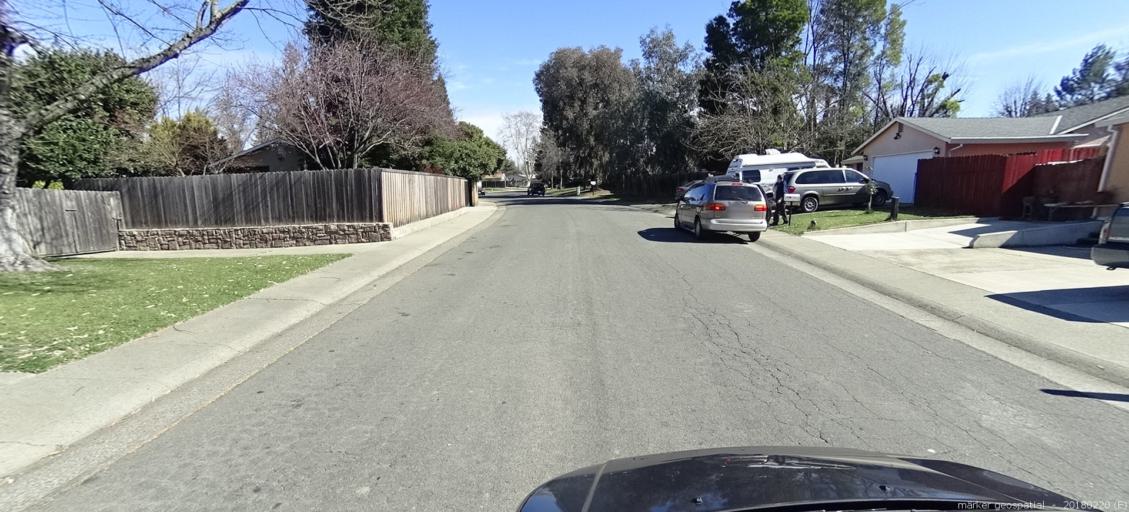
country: US
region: California
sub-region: Sacramento County
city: Orangevale
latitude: 38.7014
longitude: -121.2347
